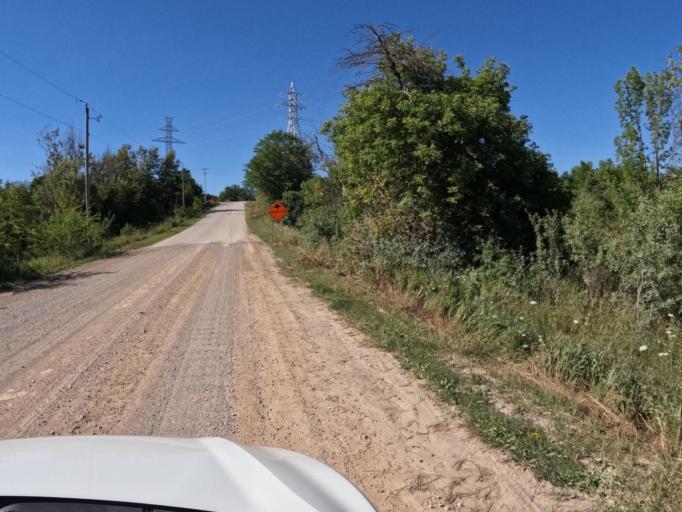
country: CA
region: Ontario
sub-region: Wellington County
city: Guelph
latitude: 43.4266
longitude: -80.1258
